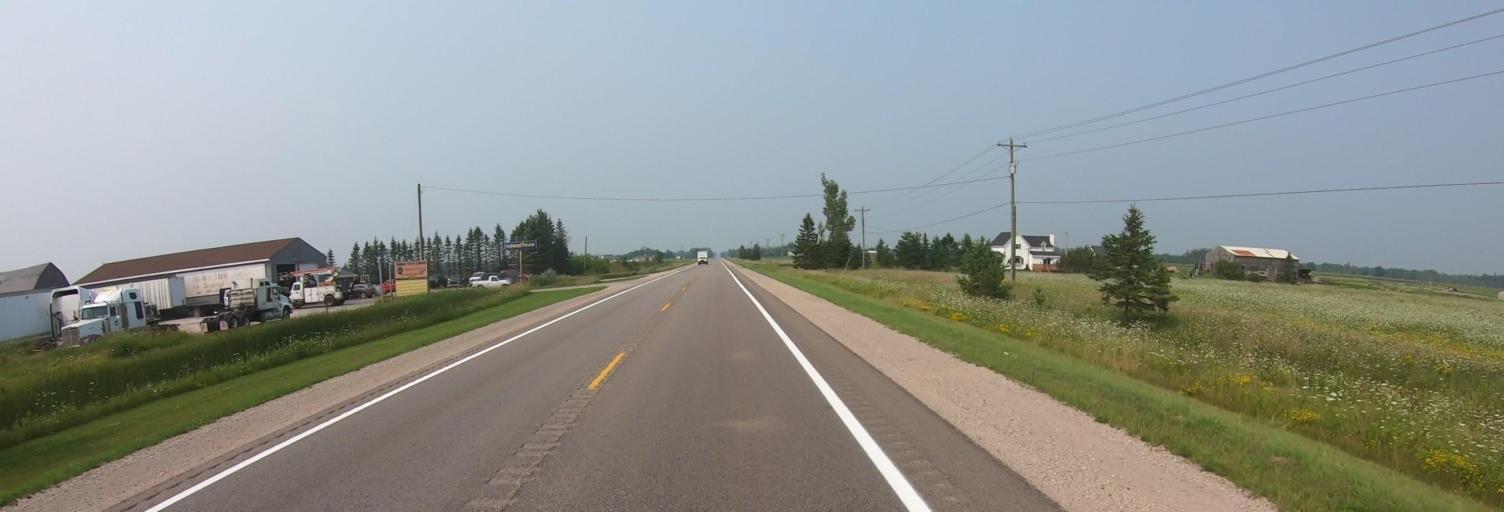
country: US
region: Michigan
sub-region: Chippewa County
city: Sault Ste. Marie
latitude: 46.1661
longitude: -84.3635
